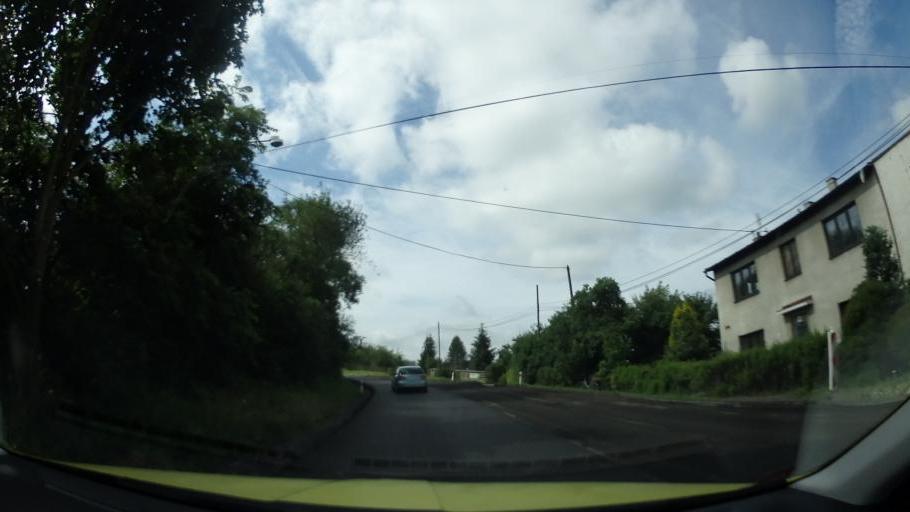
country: CZ
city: Hodslavice
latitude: 49.5554
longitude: 18.0219
